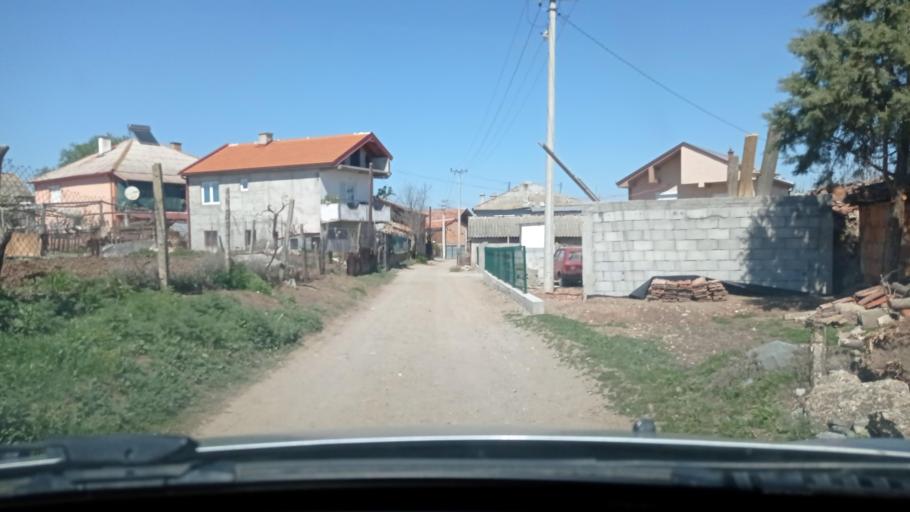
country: MK
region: Lozovo
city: Lozovo
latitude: 41.7629
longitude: 21.8648
